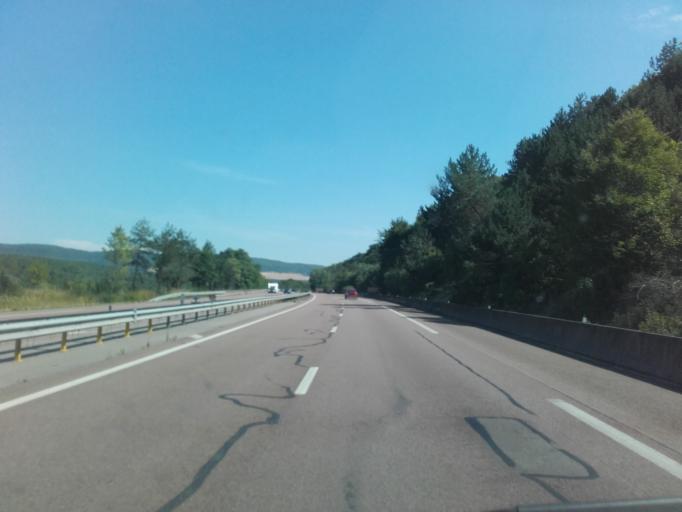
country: FR
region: Bourgogne
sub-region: Departement de la Cote-d'Or
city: Pouilly-en-Auxois
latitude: 47.1782
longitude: 4.6829
